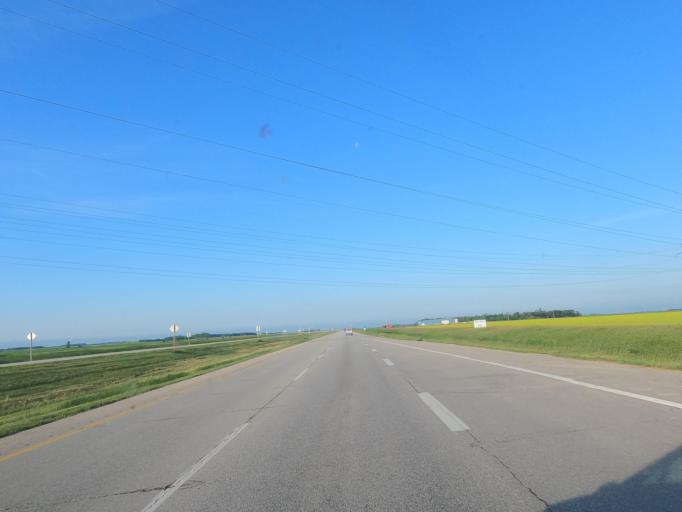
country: CA
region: Manitoba
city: Headingley
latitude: 49.9853
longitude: -97.3128
